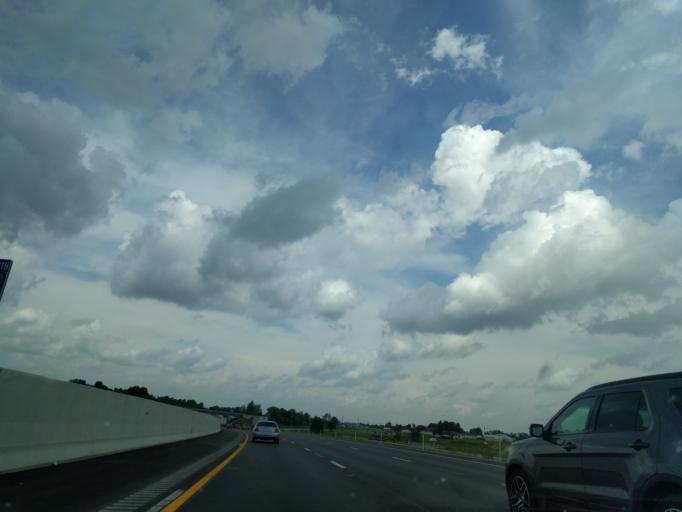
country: US
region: Kentucky
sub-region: Larue County
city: Hodgenville
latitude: 37.4946
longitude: -85.8818
